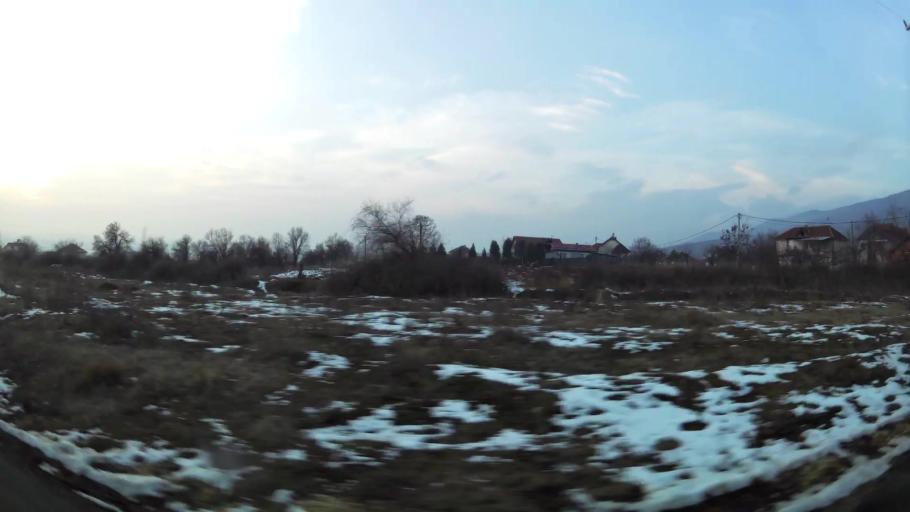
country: MK
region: Aracinovo
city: Arachinovo
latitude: 42.0315
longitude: 21.5481
